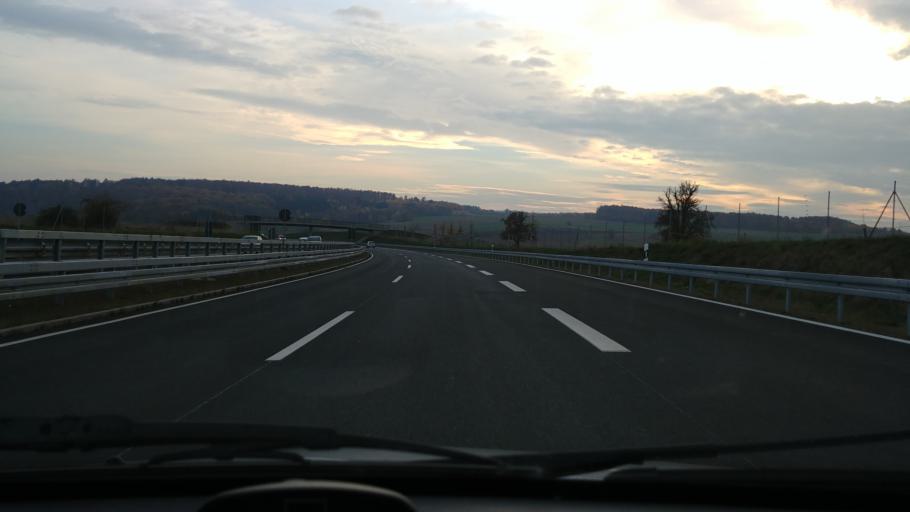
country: DE
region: Hesse
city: Merenberg
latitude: 50.4860
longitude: 8.1695
